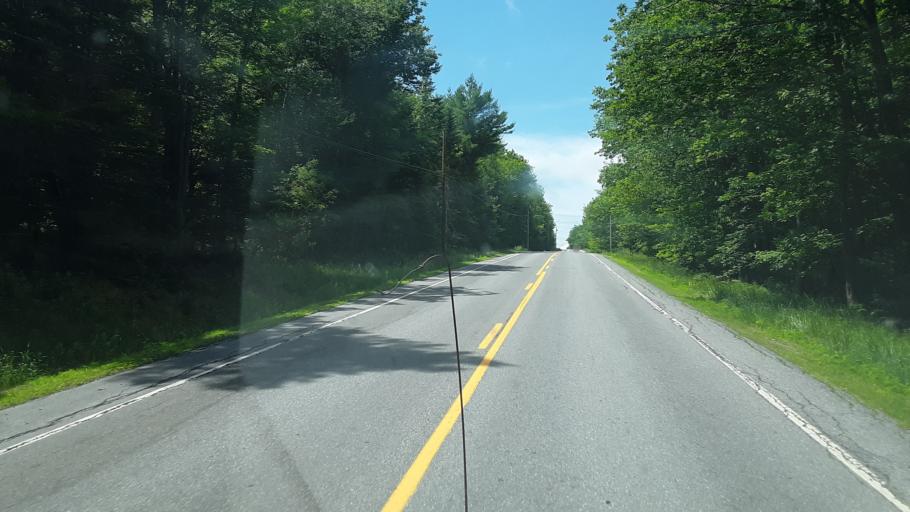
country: US
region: Maine
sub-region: Hancock County
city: Bucksport
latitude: 44.5695
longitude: -68.8258
